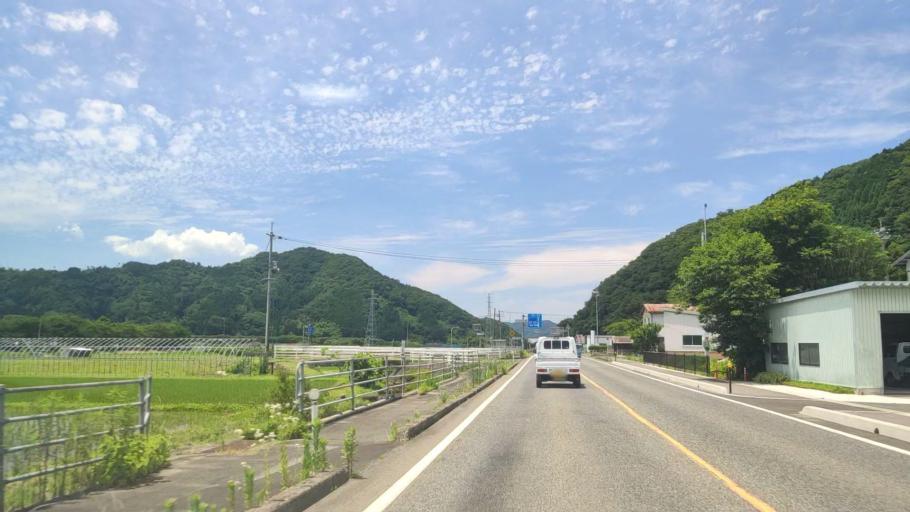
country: JP
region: Tottori
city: Tottori
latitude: 35.3768
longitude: 134.2976
